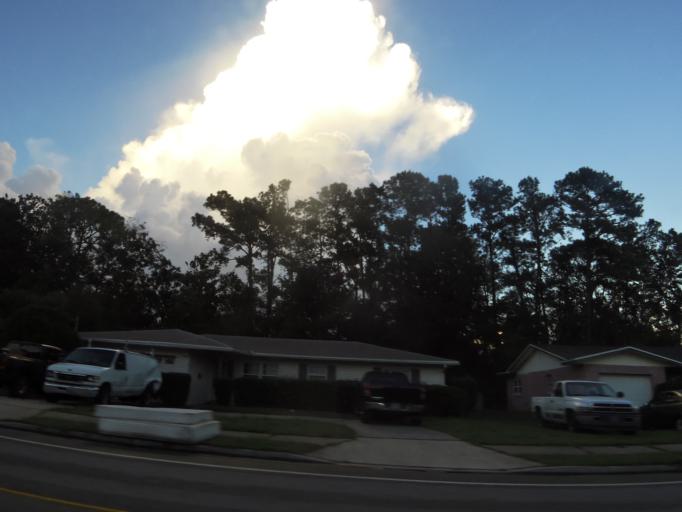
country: US
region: Florida
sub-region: Duval County
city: Jacksonville
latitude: 30.2362
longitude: -81.6063
